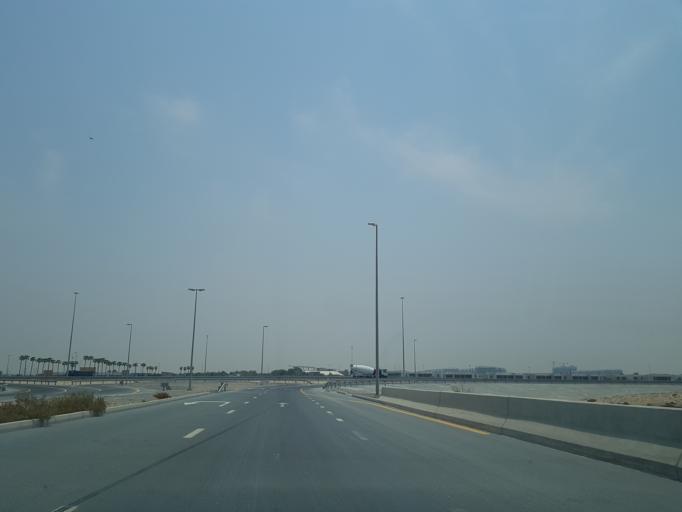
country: AE
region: Dubai
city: Dubai
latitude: 25.0314
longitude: 55.2499
